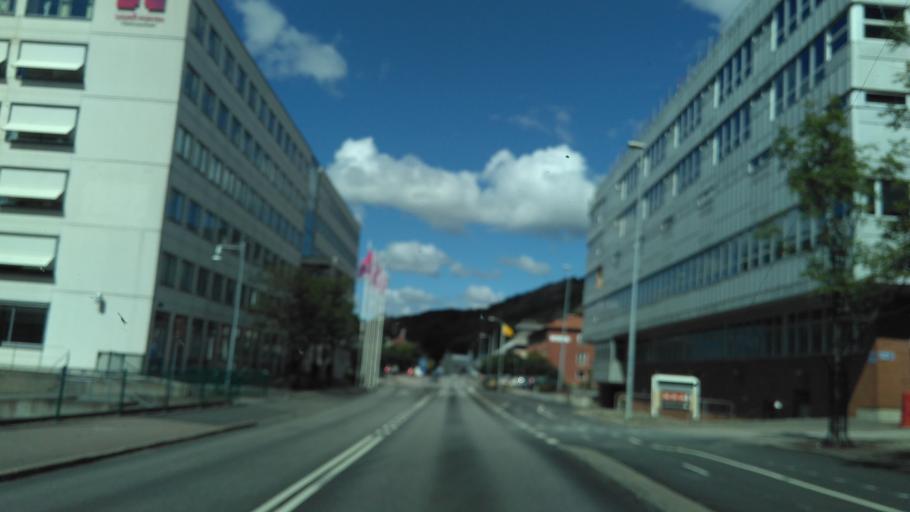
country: SE
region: Vaestra Goetaland
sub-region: Molndal
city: Moelndal
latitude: 57.6667
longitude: 12.0172
